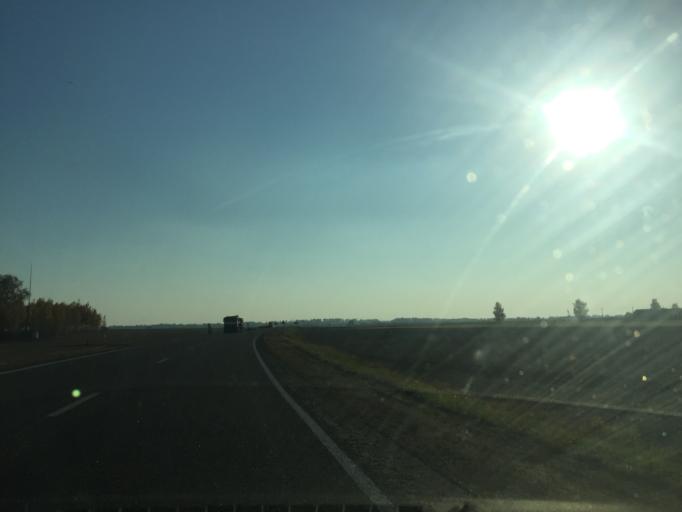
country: BY
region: Gomel
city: Dobrush
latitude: 52.3191
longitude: 31.2462
